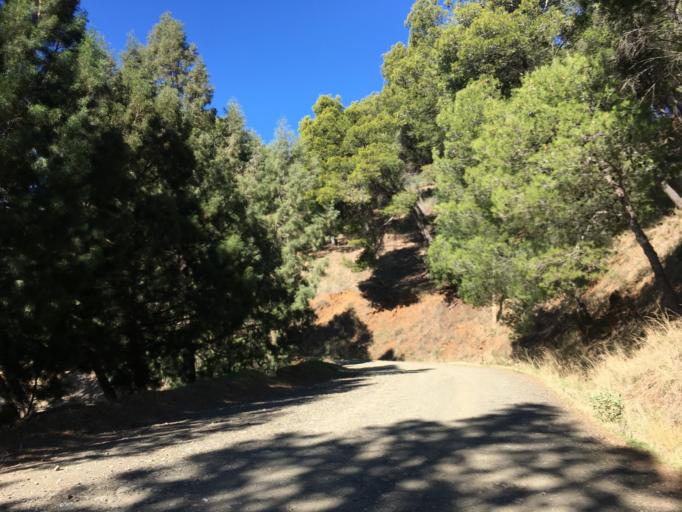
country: ES
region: Andalusia
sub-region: Provincia de Malaga
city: Malaga
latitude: 36.7824
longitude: -4.3891
